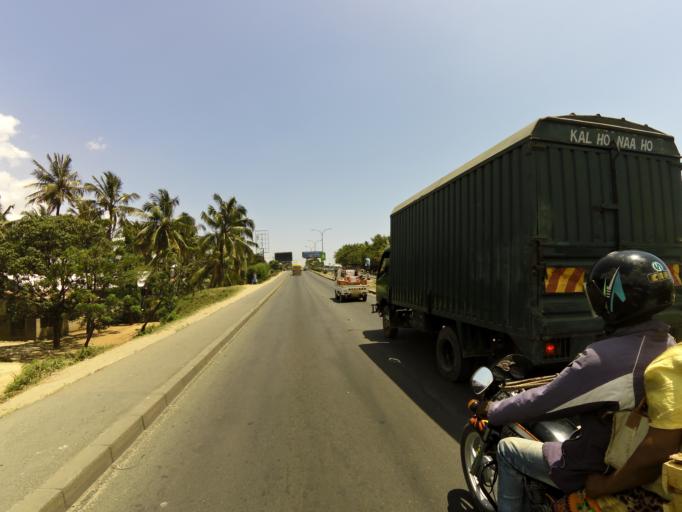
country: TZ
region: Dar es Salaam
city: Dar es Salaam
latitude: -6.8183
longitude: 39.2556
